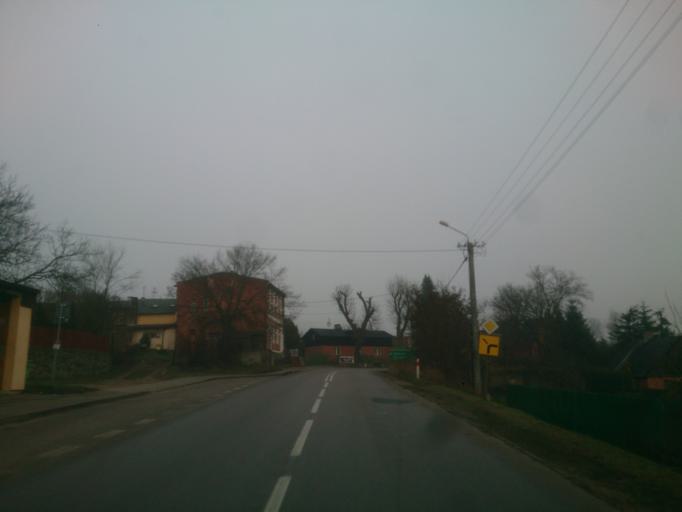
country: PL
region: Pomeranian Voivodeship
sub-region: Powiat starogardzki
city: Zblewo
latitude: 53.8871
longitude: 18.3499
